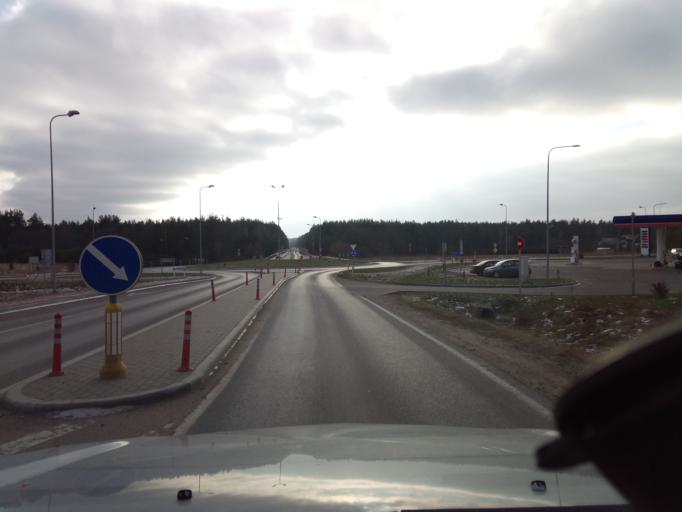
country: LT
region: Alytaus apskritis
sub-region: Alytaus rajonas
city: Daugai
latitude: 54.1696
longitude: 24.2082
